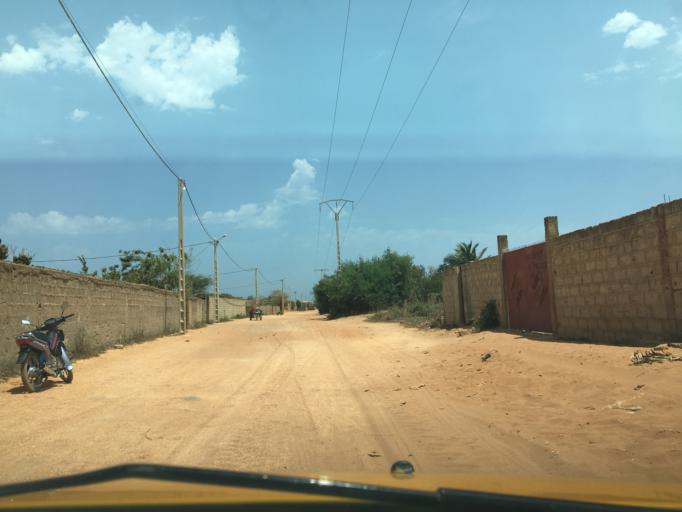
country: SN
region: Thies
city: Thies
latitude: 14.8094
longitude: -17.1898
